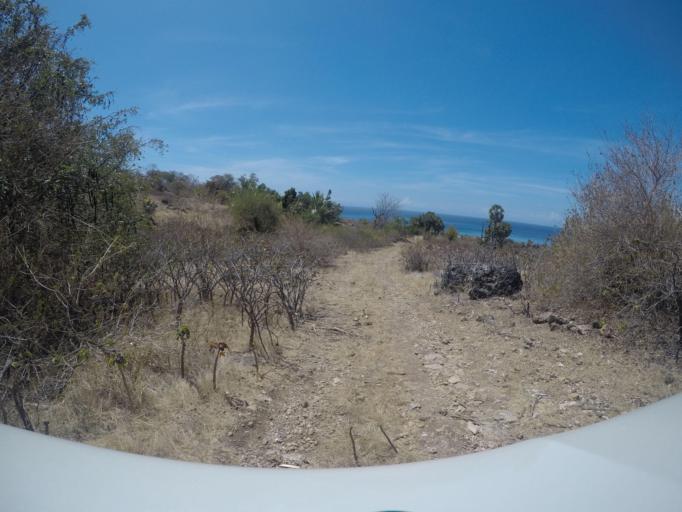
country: TL
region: Baucau
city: Baucau
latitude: -8.4364
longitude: 126.4390
